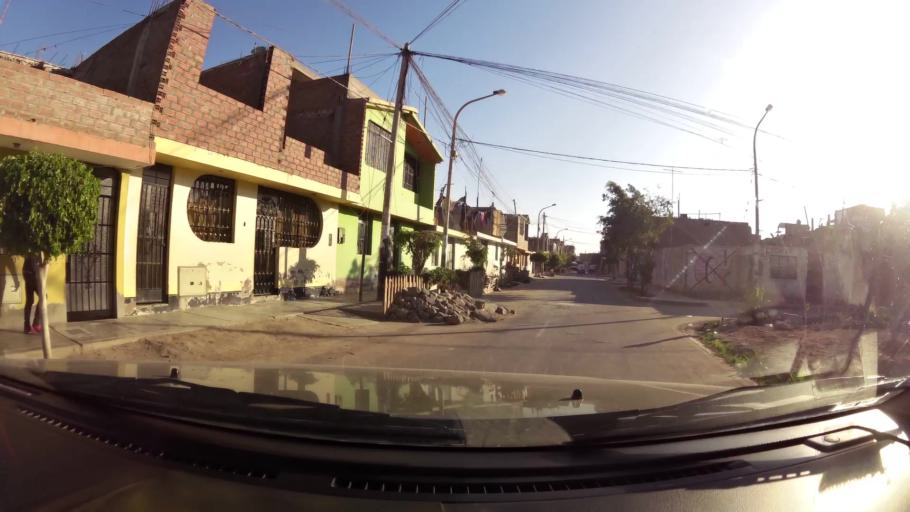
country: PE
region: Ica
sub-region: Provincia de Ica
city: Ica
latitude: -14.0709
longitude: -75.7164
